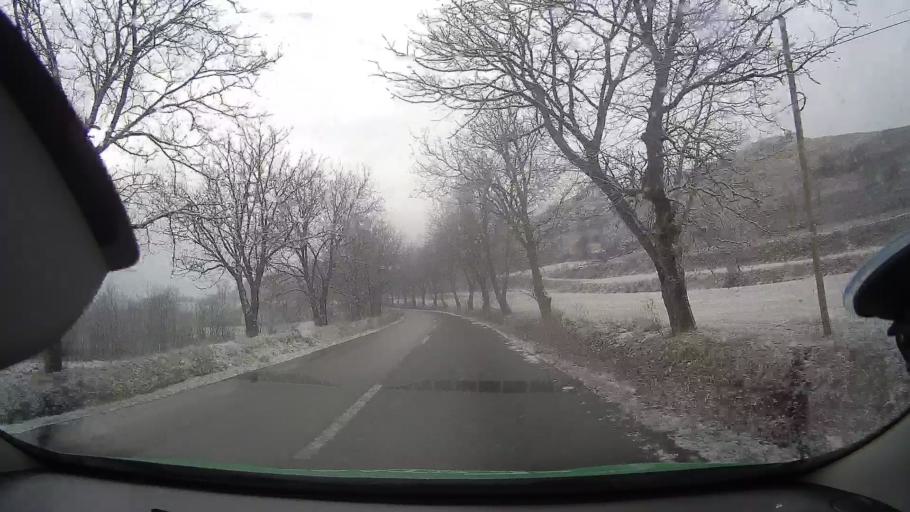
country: RO
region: Alba
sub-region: Comuna Rimetea
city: Rimetea
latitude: 46.4389
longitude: 23.5627
